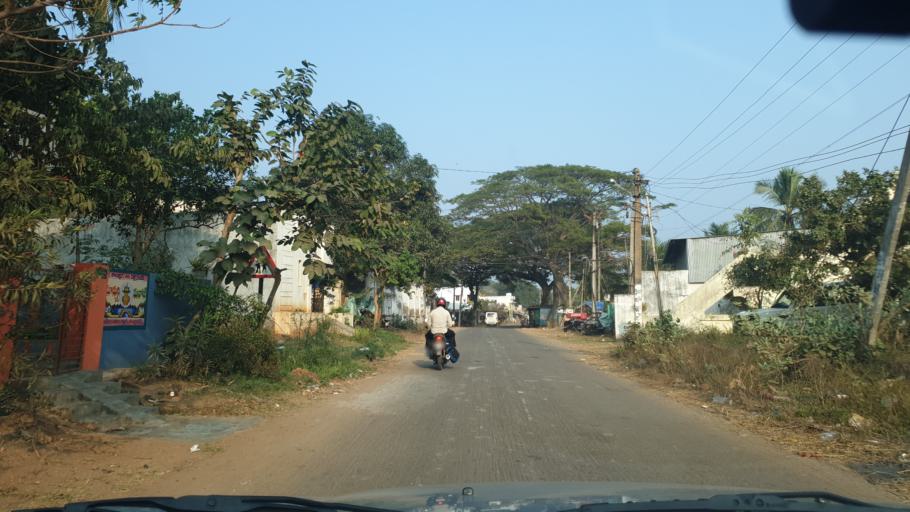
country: IN
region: Andhra Pradesh
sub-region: Srikakulam
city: Narasannapeta
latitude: 18.3312
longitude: 84.0371
